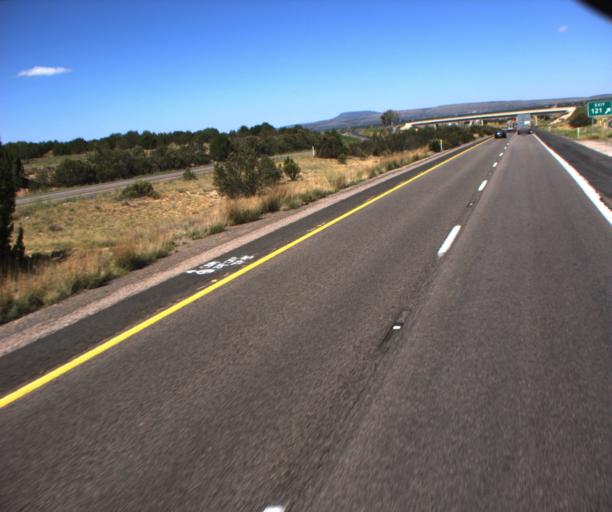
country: US
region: Arizona
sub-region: Mohave County
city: Peach Springs
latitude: 35.3197
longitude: -112.8894
